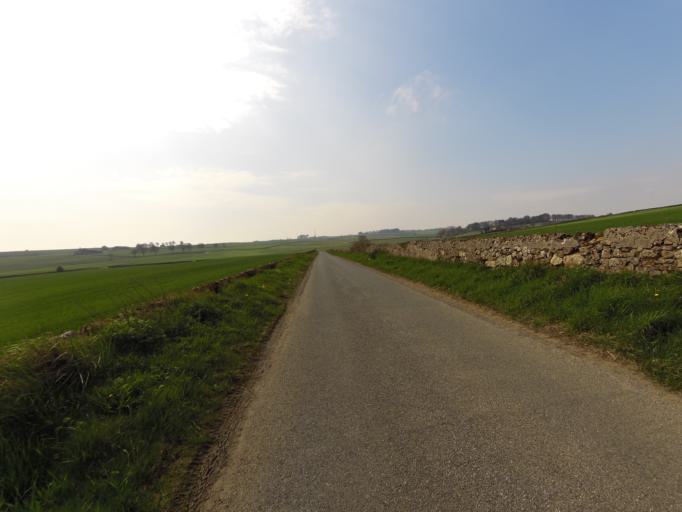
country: GB
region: Scotland
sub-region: Fife
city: Kinghorn
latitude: 56.0900
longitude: -3.1799
